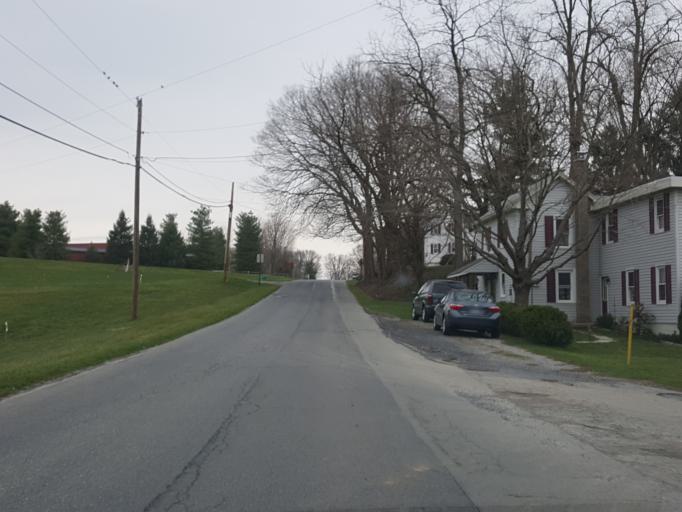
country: US
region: Pennsylvania
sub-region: Lancaster County
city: Marietta
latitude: 40.0596
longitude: -76.5515
